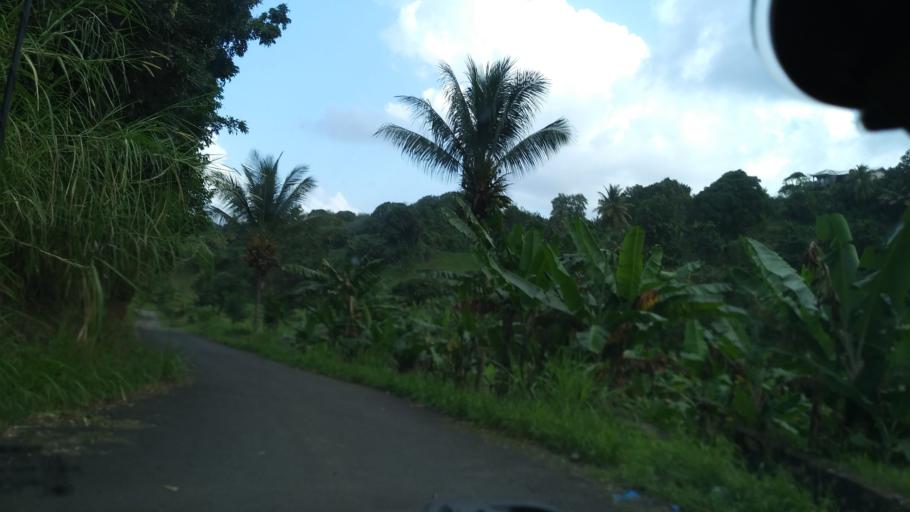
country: VC
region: Charlotte
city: Byera Village
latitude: 13.2317
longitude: -61.1345
